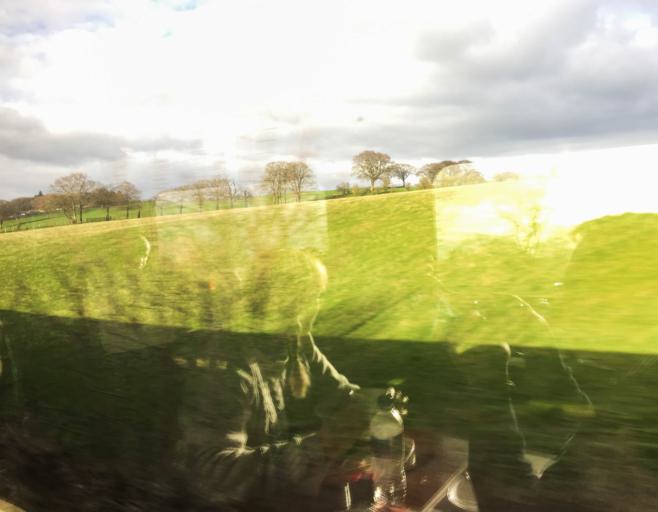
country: GB
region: Scotland
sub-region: Dumfries and Galloway
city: Lockerbie
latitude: 55.1111
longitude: -3.3494
